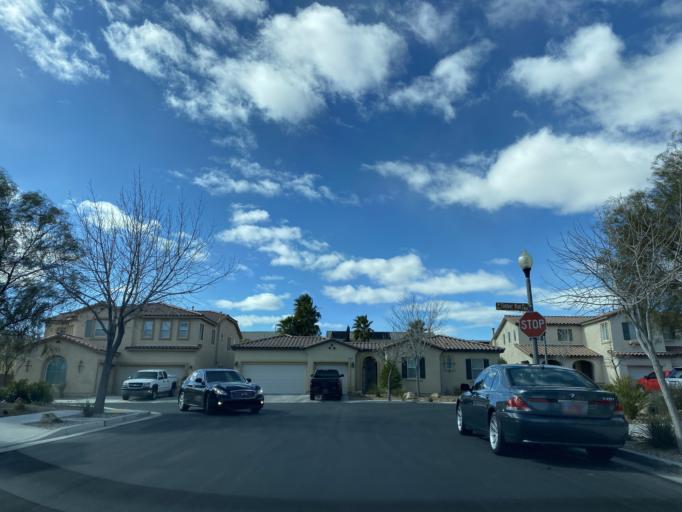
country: US
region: Nevada
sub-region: Clark County
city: Summerlin South
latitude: 36.2968
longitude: -115.3029
